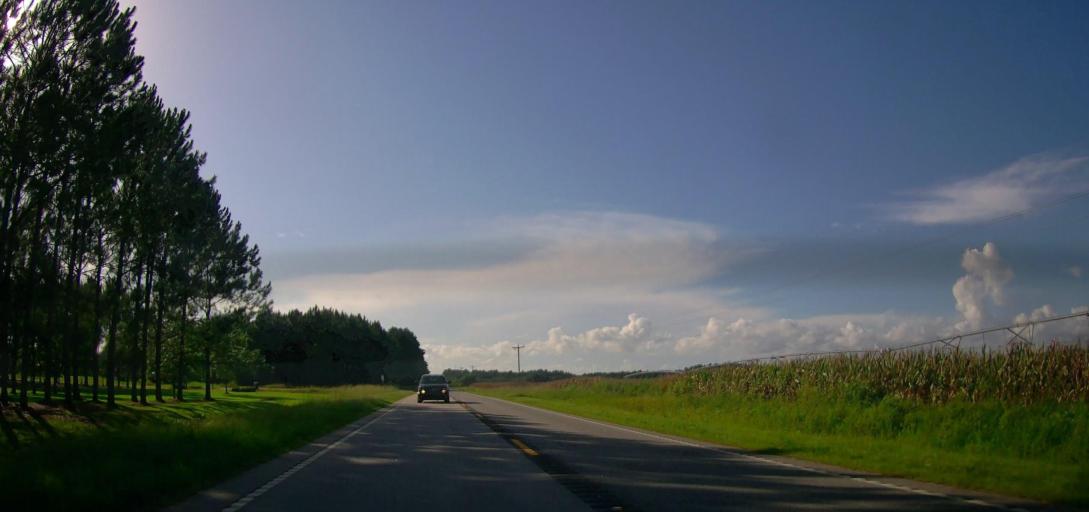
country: US
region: Georgia
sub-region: Coffee County
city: Nicholls
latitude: 31.4340
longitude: -82.7079
